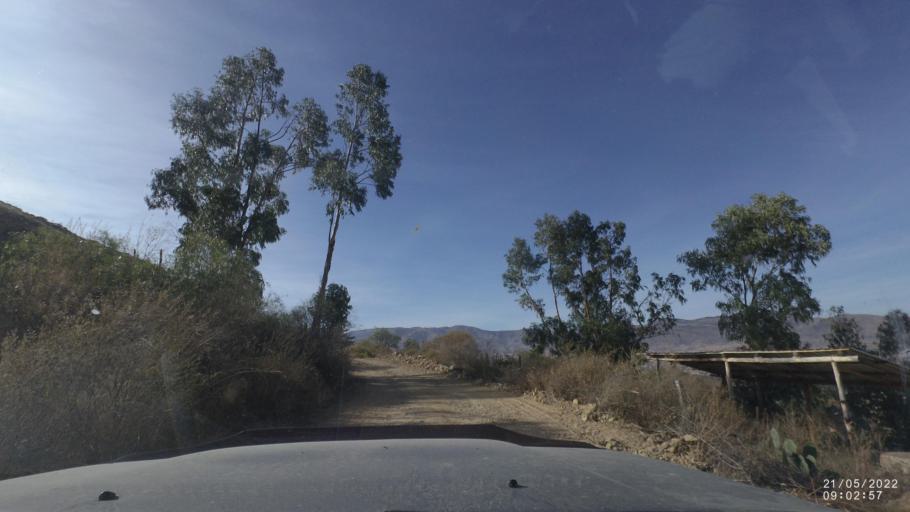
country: BO
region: Cochabamba
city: Cochabamba
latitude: -17.3784
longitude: -66.0297
